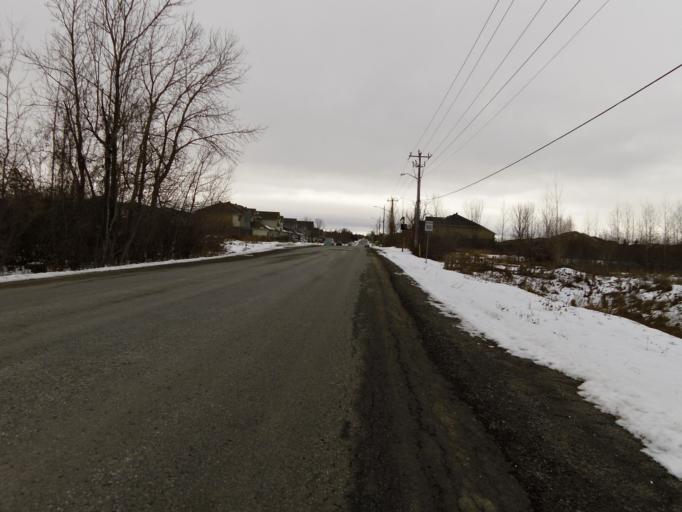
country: CA
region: Ontario
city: Bells Corners
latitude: 45.3611
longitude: -75.9232
